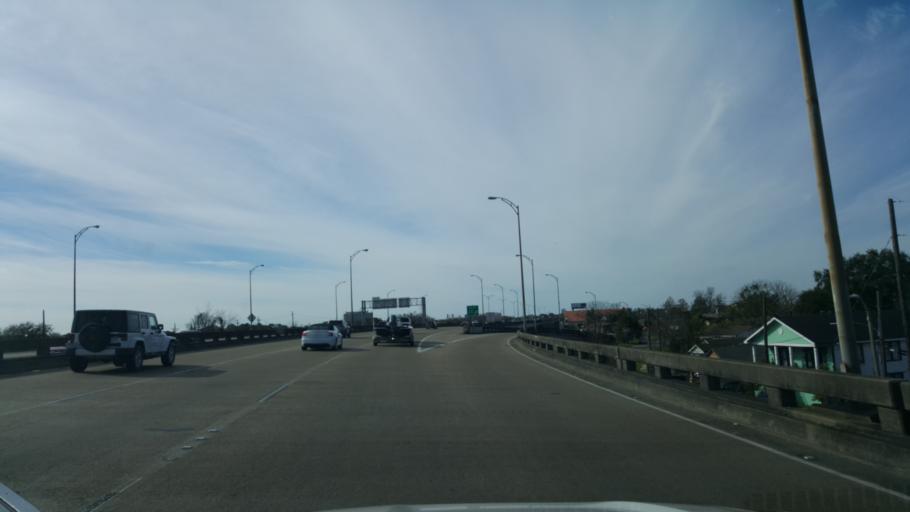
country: US
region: Louisiana
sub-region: Orleans Parish
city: New Orleans
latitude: 29.9909
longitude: -90.0696
